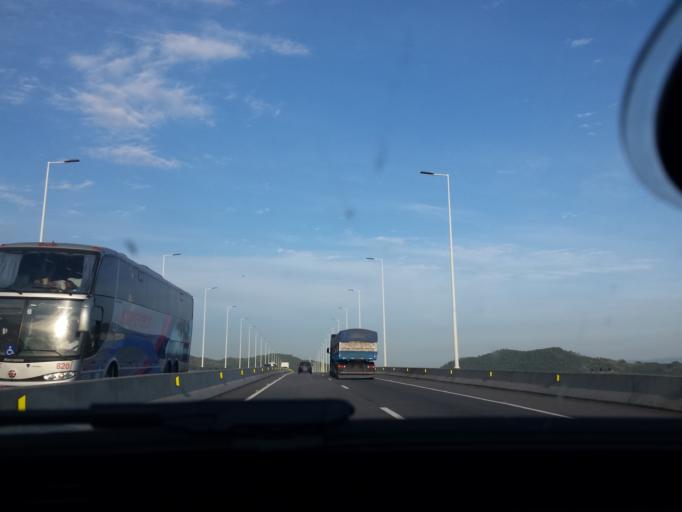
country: BR
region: Santa Catarina
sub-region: Laguna
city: Laguna
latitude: -28.4402
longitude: -48.8259
